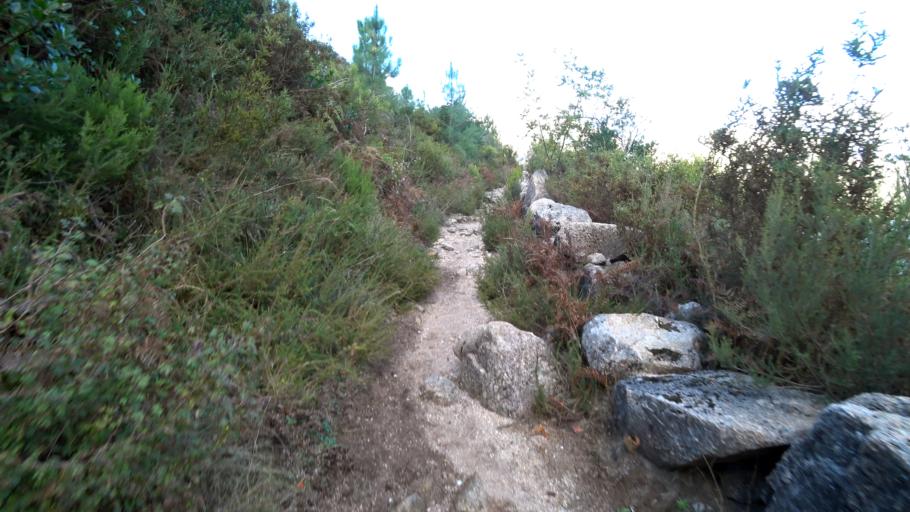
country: PT
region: Braga
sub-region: Terras de Bouro
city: Antas
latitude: 41.7703
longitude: -8.1870
